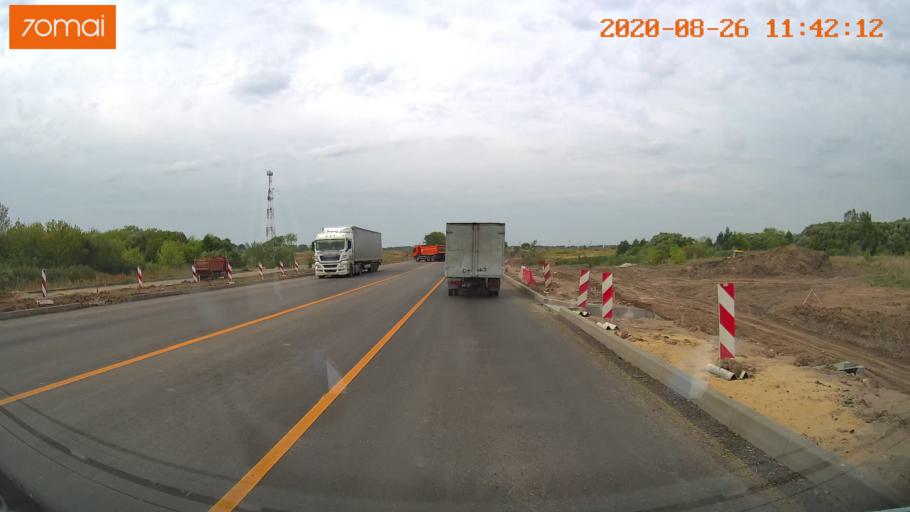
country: RU
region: Rjazan
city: Shilovo
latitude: 54.2969
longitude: 40.6978
